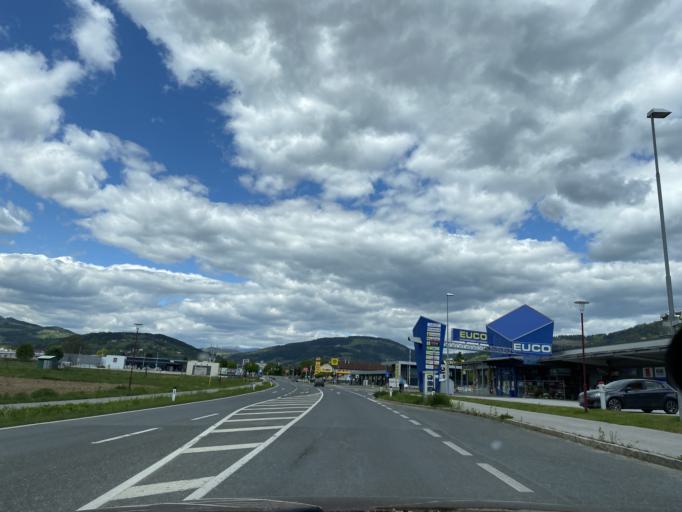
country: AT
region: Carinthia
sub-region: Politischer Bezirk Wolfsberg
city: Wolfsberg
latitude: 46.8247
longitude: 14.8394
